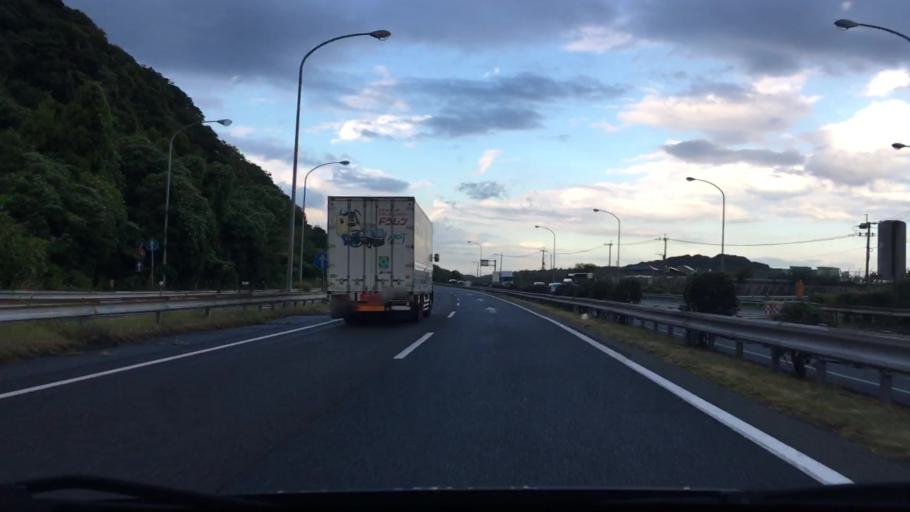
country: JP
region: Yamaguchi
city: Shimonoseki
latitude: 33.8733
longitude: 130.9660
